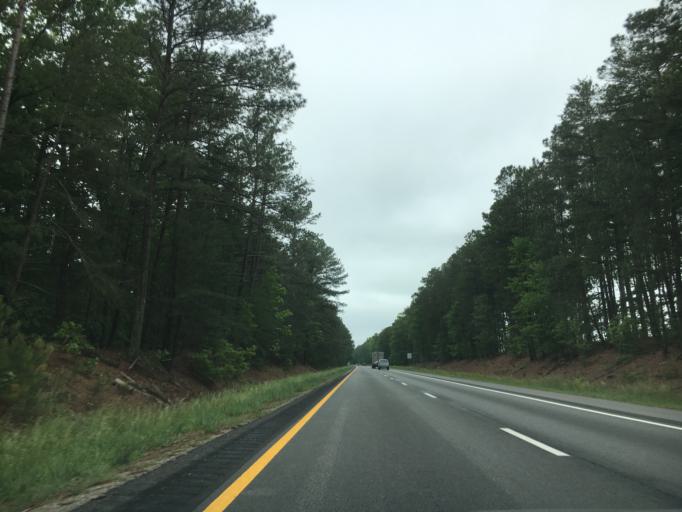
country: US
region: Virginia
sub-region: Dinwiddie County
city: Dinwiddie
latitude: 37.0288
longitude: -77.6403
